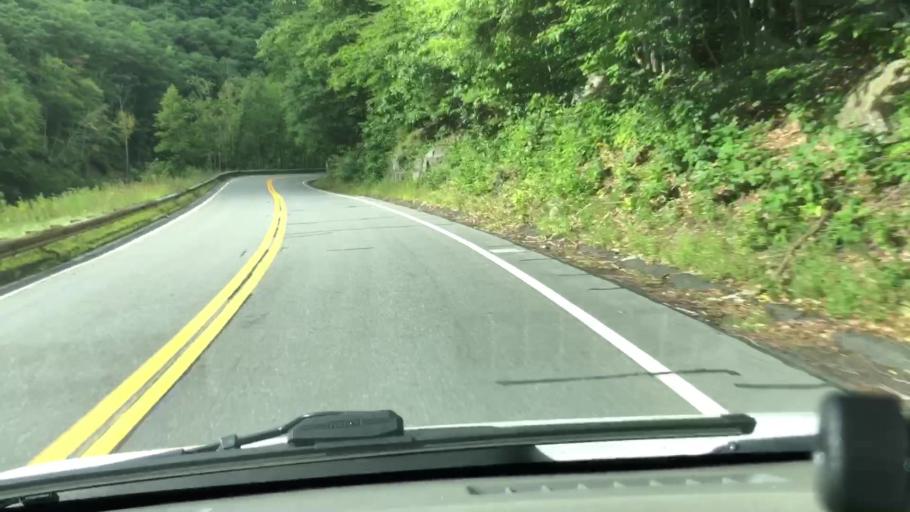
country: US
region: Massachusetts
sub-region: Franklin County
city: Charlemont
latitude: 42.6348
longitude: -72.9660
